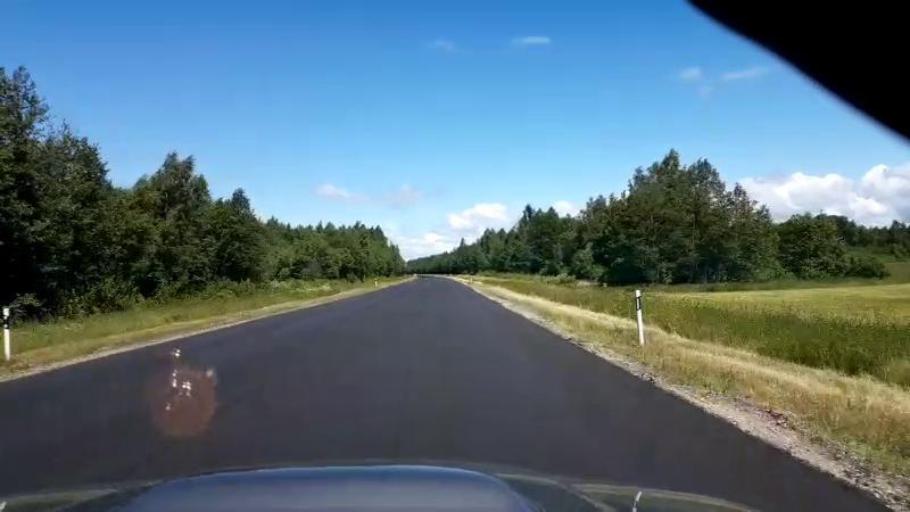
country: LV
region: Salacgrivas
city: Ainazi
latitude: 57.9081
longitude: 24.4168
